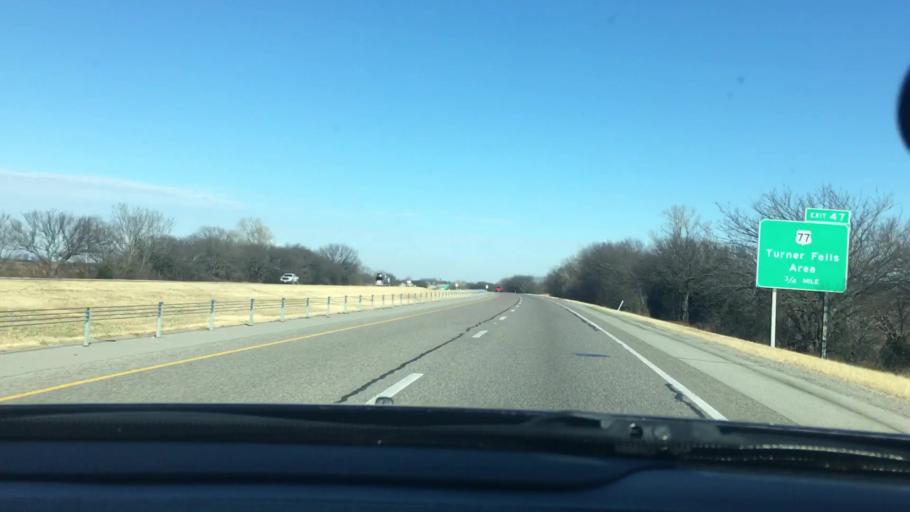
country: US
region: Oklahoma
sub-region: Murray County
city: Davis
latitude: 34.3841
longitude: -97.1420
